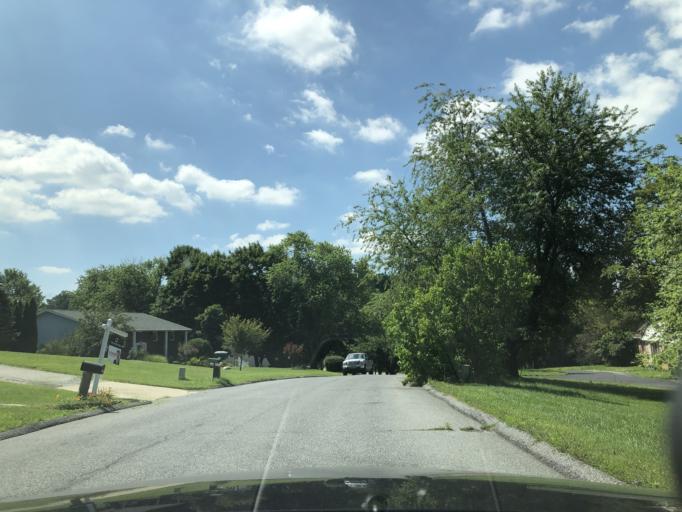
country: US
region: Maryland
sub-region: Carroll County
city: Westminster
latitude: 39.6189
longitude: -77.0032
